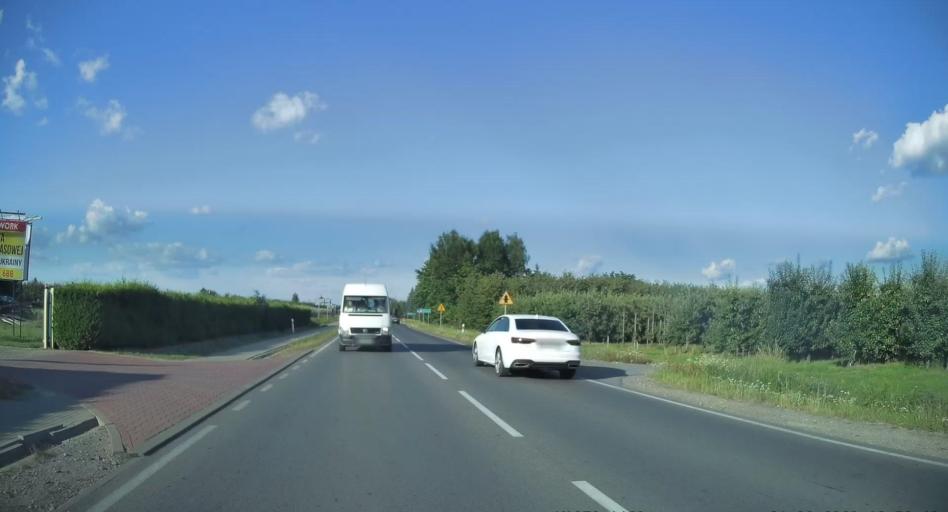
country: PL
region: Masovian Voivodeship
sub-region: Powiat grojecki
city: Belsk Duzy
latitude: 51.8437
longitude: 20.8323
